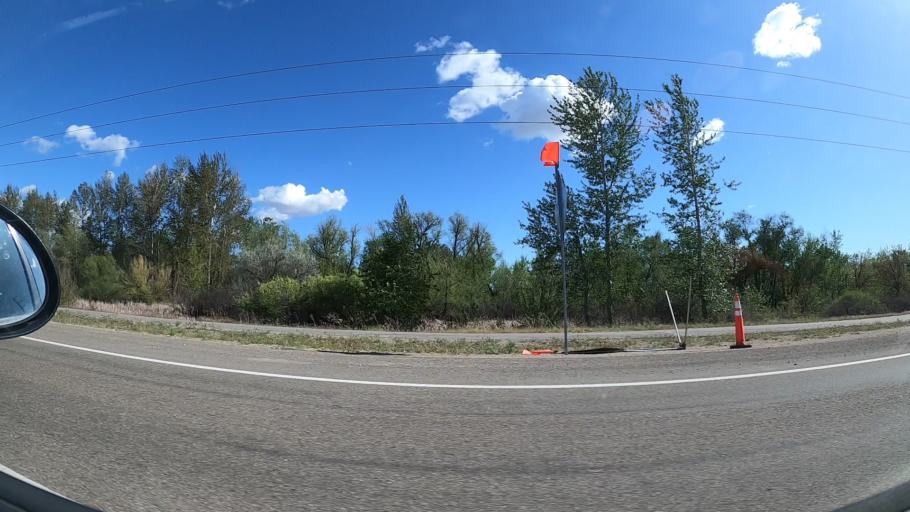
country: US
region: Idaho
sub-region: Ada County
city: Eagle
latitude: 43.6919
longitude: -116.3688
